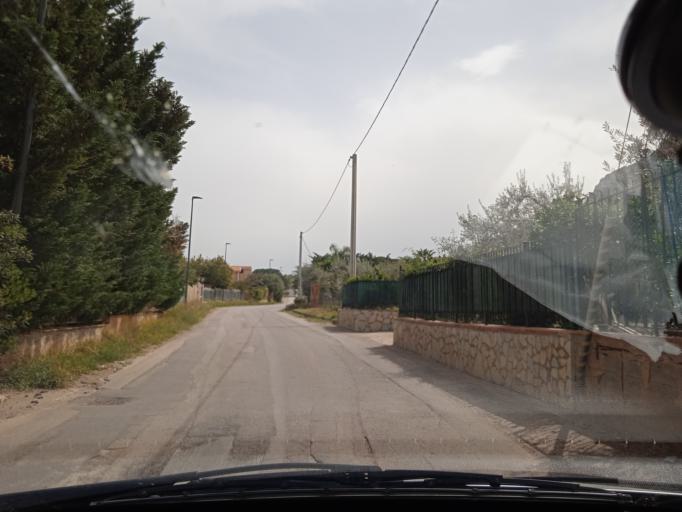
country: IT
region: Sicily
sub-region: Palermo
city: Torre Colonna-Sperone
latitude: 38.0266
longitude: 13.5746
